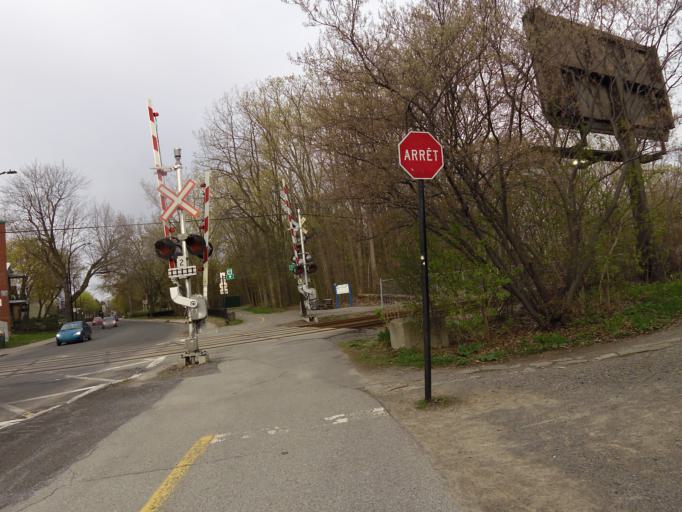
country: CA
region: Quebec
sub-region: Laval
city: Laval
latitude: 45.5462
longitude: -73.6973
